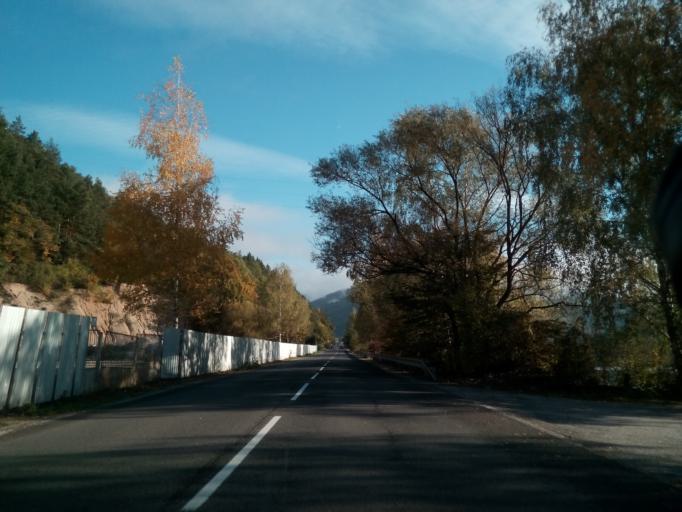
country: SK
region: Kosicky
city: Gelnica
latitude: 48.8850
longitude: 21.0027
